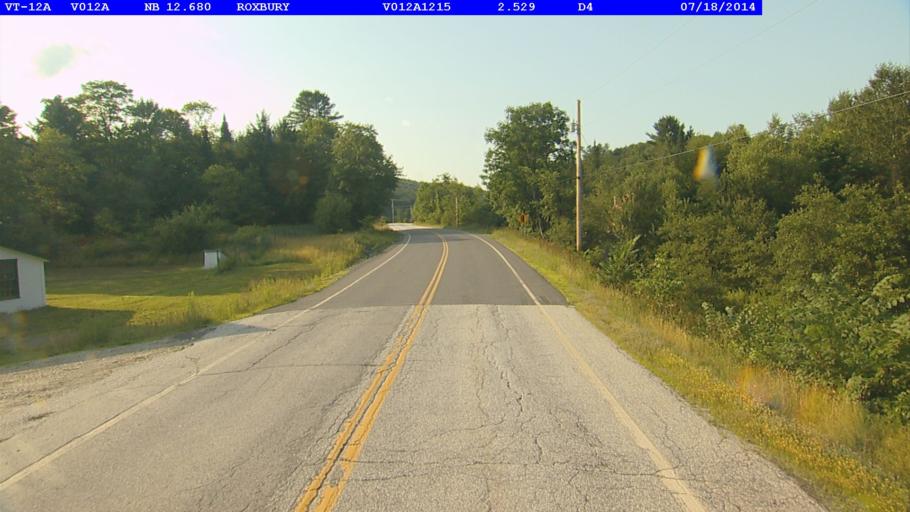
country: US
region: Vermont
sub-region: Washington County
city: Northfield
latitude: 44.0649
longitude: -72.7439
